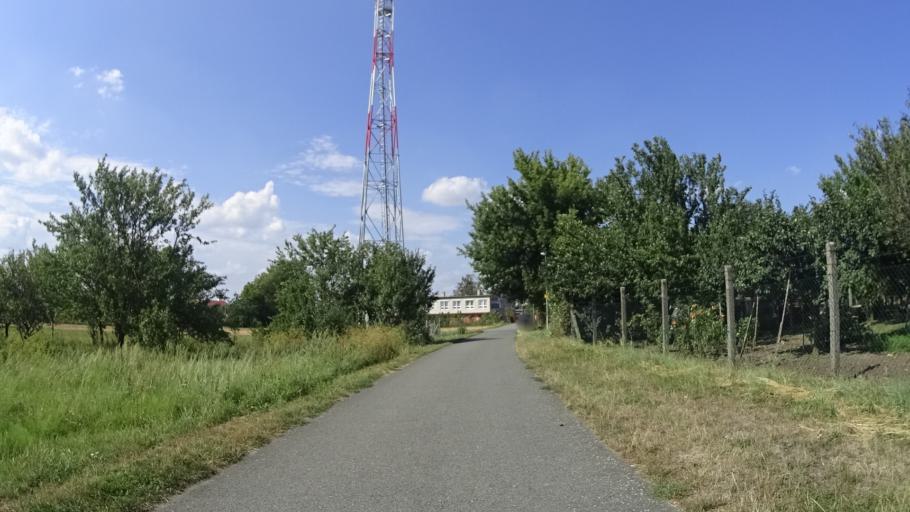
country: CZ
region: Zlin
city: Uhersky Ostroh
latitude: 48.9807
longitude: 17.3966
